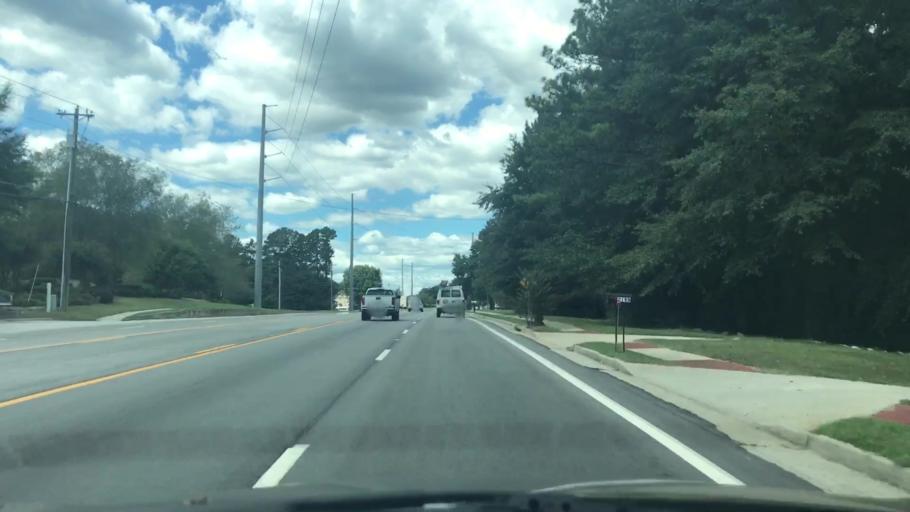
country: US
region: Georgia
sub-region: Gwinnett County
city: Mountain Park
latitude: 33.8188
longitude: -84.1086
